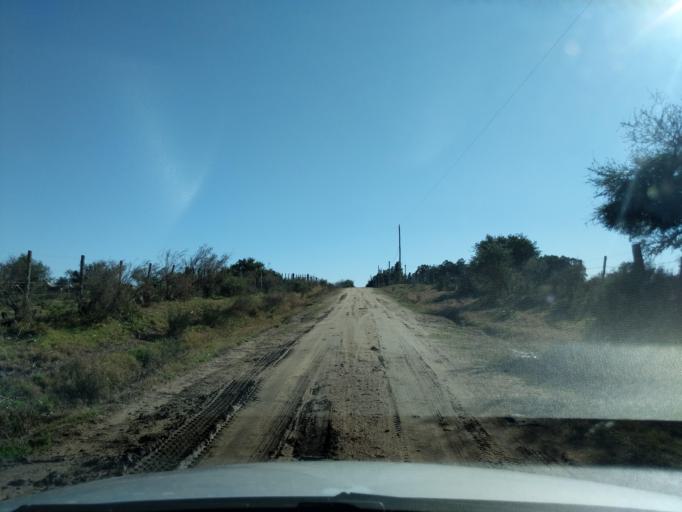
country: UY
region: Florida
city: Florida
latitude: -34.0779
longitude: -56.2680
